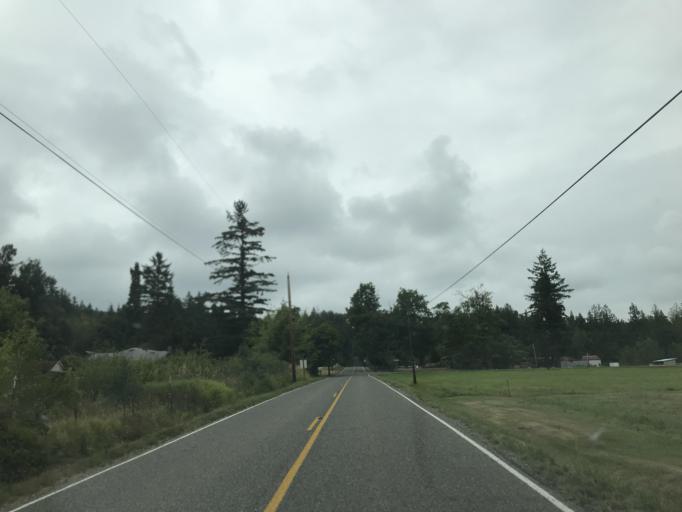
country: US
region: Washington
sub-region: Whatcom County
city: Sudden Valley
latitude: 48.7906
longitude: -122.3330
